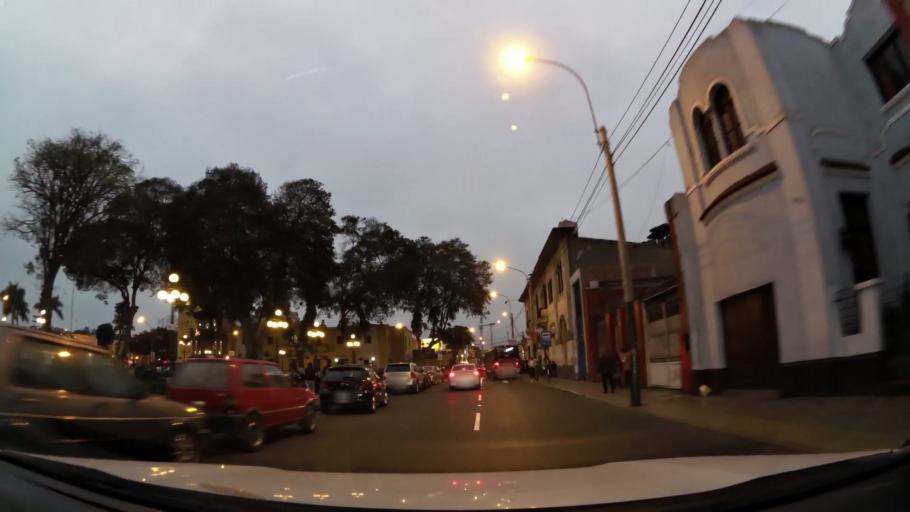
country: PE
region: Lima
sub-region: Lima
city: Surco
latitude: -12.1495
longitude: -77.0208
